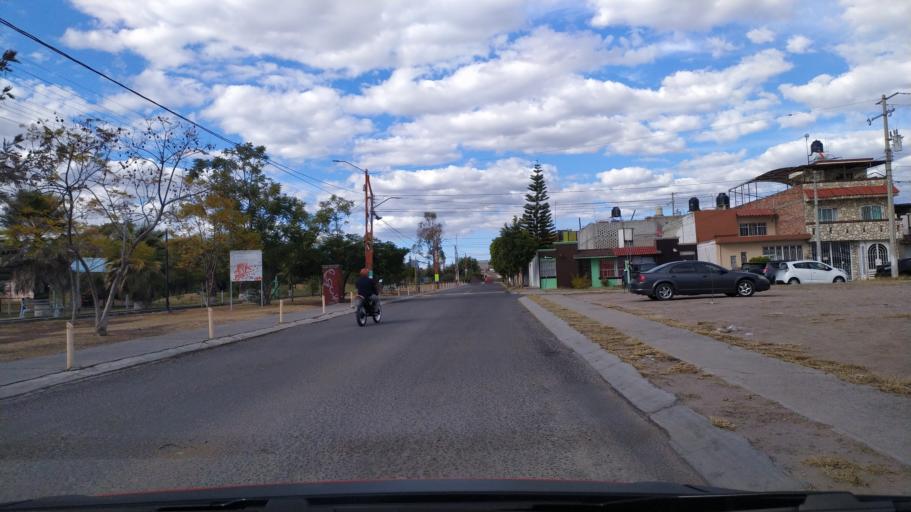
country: MX
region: Guanajuato
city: San Francisco del Rincon
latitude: 21.0368
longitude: -101.8486
